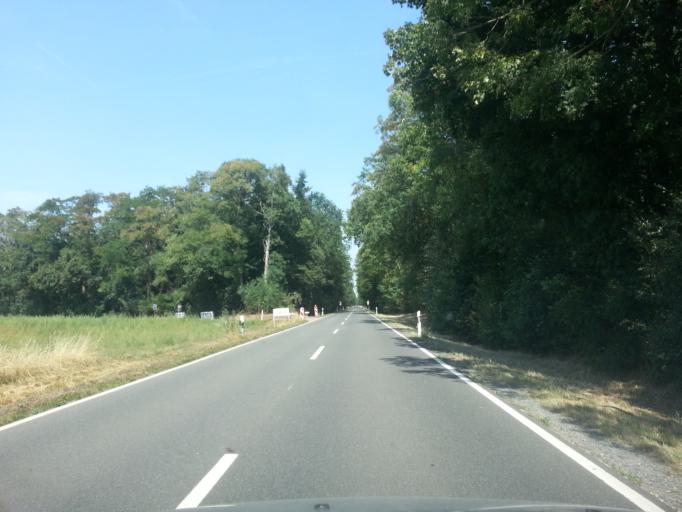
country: DE
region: Hesse
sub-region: Regierungsbezirk Darmstadt
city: Einhausen
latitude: 49.6824
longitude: 8.5331
